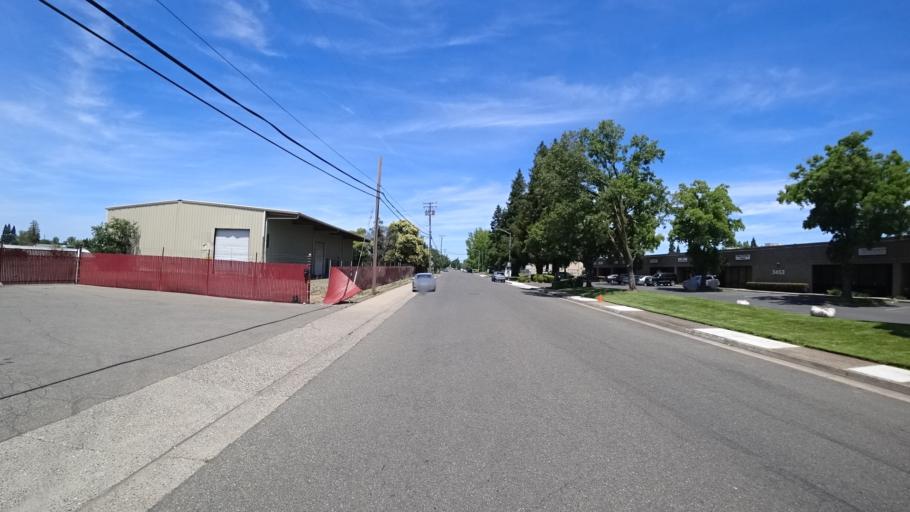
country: US
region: California
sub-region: Sacramento County
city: Florin
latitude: 38.5424
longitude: -121.4122
